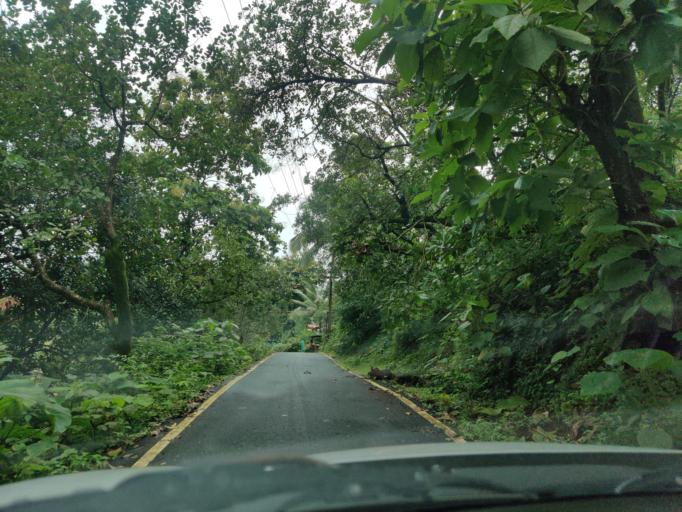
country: IN
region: Goa
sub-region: North Goa
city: Valpoy
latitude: 15.5284
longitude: 74.1423
